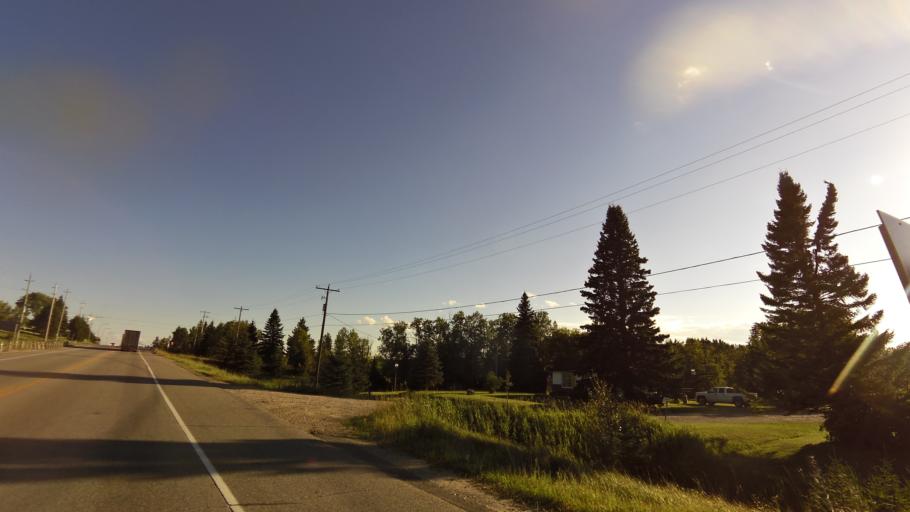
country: CA
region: Ontario
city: Dryden
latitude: 49.8023
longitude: -92.8475
